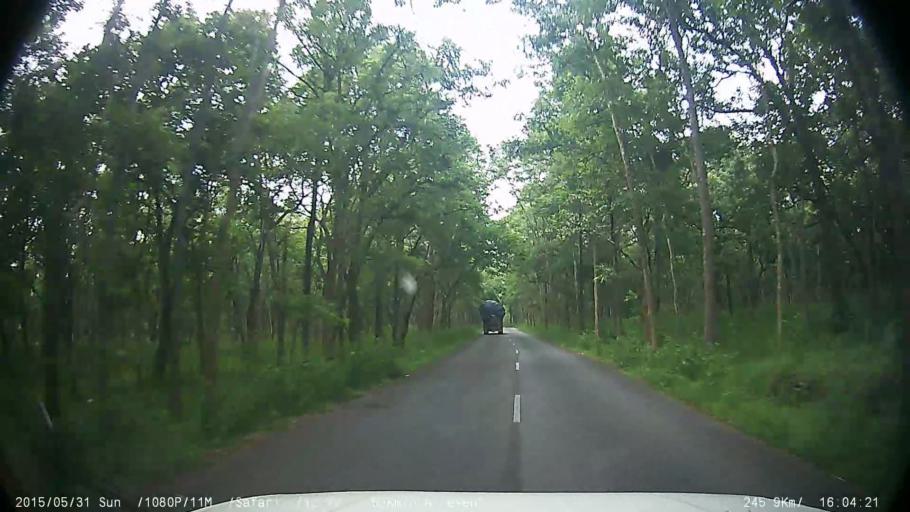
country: IN
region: Tamil Nadu
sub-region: Nilgiri
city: Naduvattam
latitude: 11.7093
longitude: 76.4154
